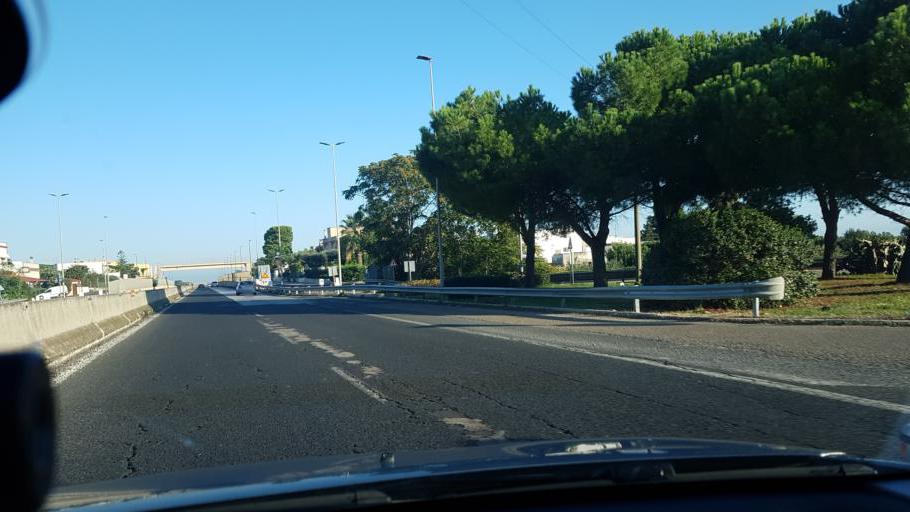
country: IT
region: Apulia
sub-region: Provincia di Brindisi
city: Fasano
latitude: 40.8817
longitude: 17.3376
